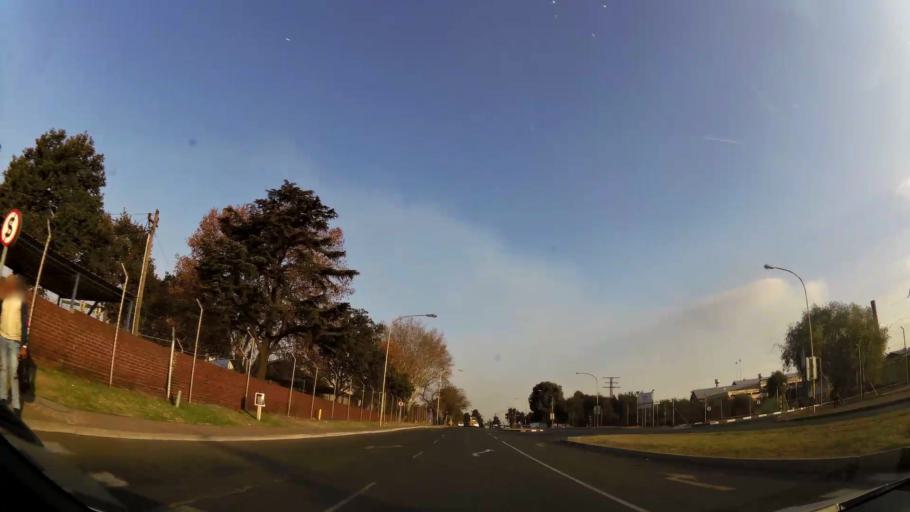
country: ZA
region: Gauteng
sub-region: Ekurhuleni Metropolitan Municipality
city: Springs
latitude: -26.2617
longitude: 28.4189
